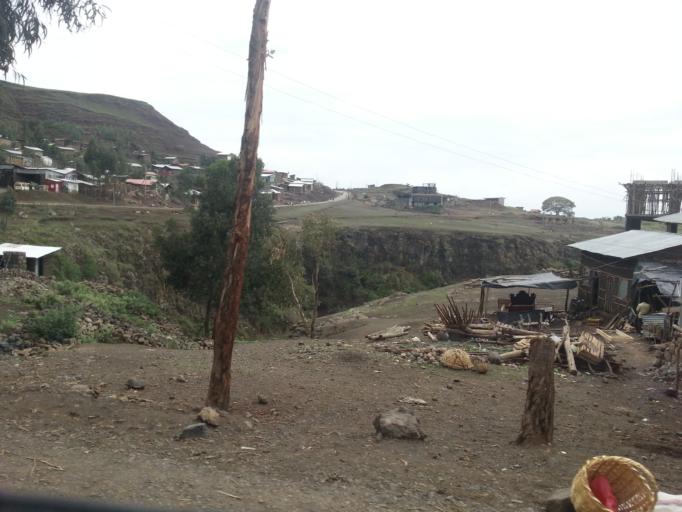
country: ET
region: Amhara
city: Lalibela
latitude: 12.0247
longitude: 39.0523
